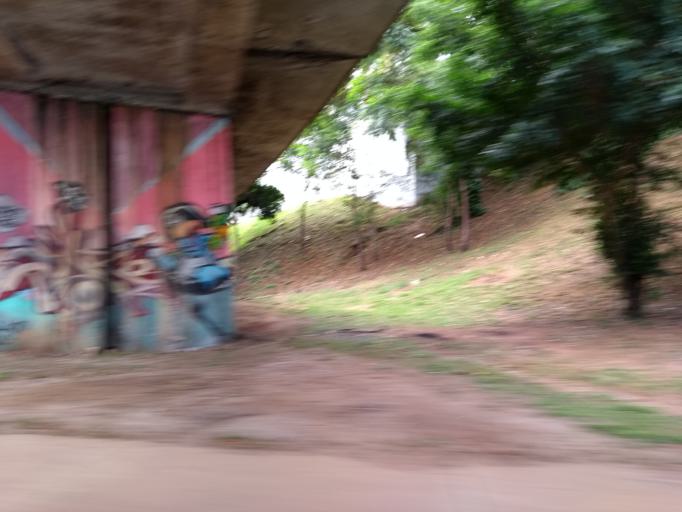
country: BR
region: Bahia
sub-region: Salvador
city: Salvador
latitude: -12.9958
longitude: -38.5239
